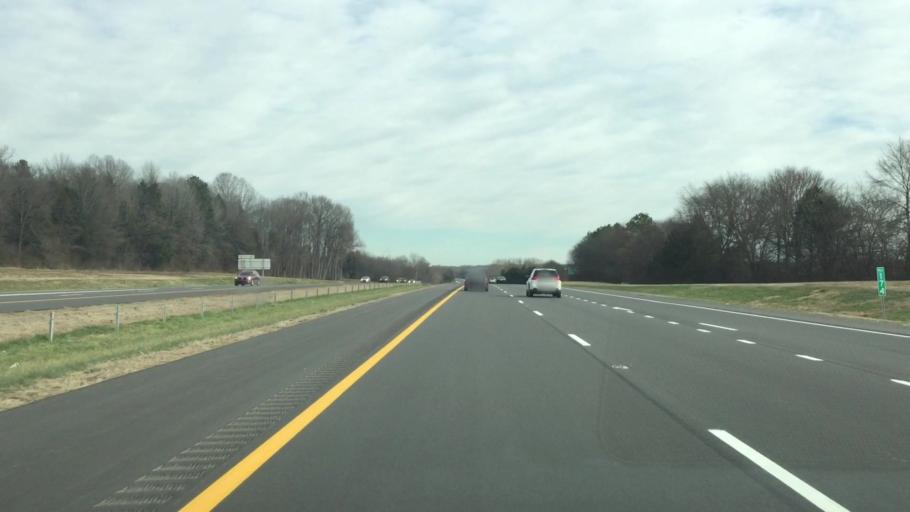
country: US
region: North Carolina
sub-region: Davie County
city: Mocksville
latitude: 35.9587
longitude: -80.5291
